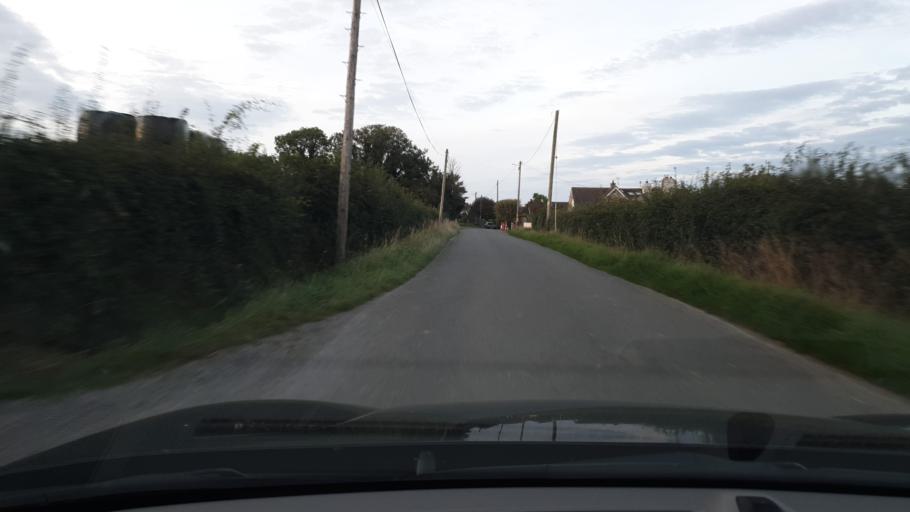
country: IE
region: Leinster
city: Balrothery
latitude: 53.5665
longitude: -6.1653
